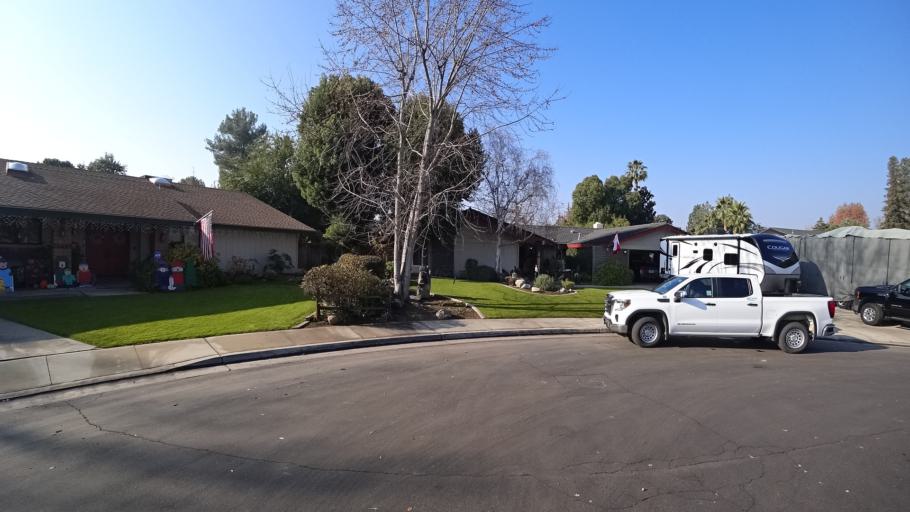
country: US
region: California
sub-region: Kern County
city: Greenacres
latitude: 35.3416
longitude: -119.0808
